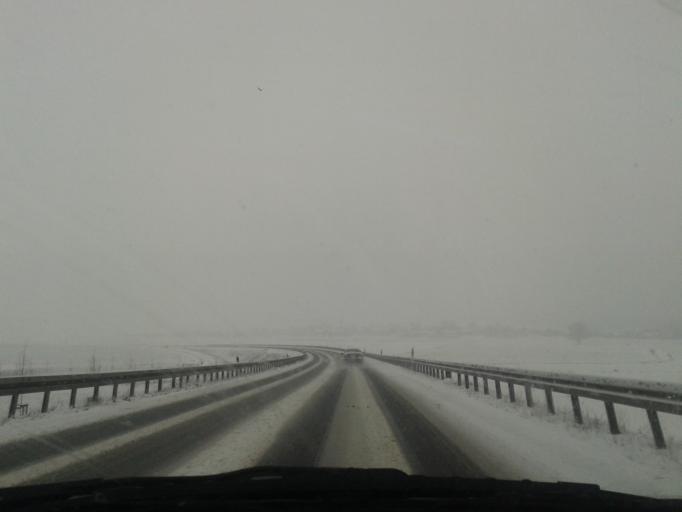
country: DE
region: Saxony
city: Bischofswerda
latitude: 51.1315
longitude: 14.1648
